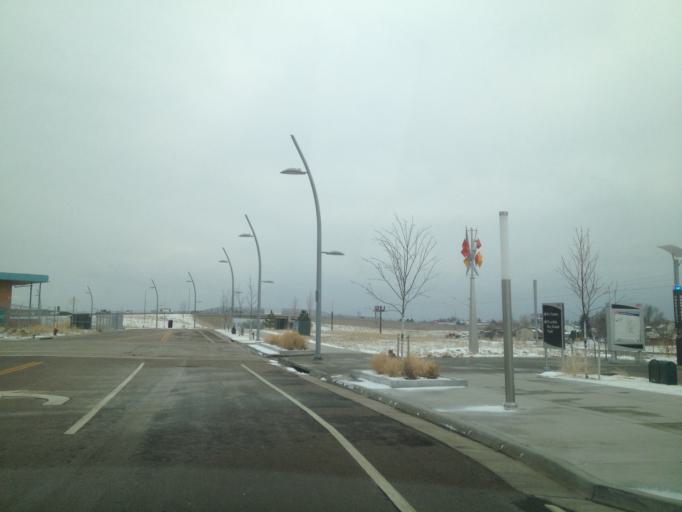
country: US
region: Colorado
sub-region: Adams County
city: Westminster
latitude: 39.8227
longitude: -105.0280
